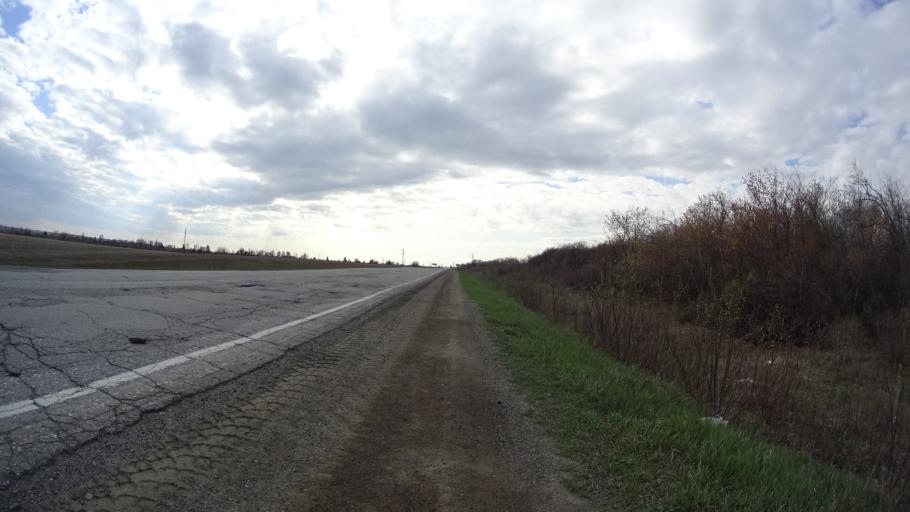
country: RU
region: Chelyabinsk
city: Troitsk
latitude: 54.0958
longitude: 61.4761
